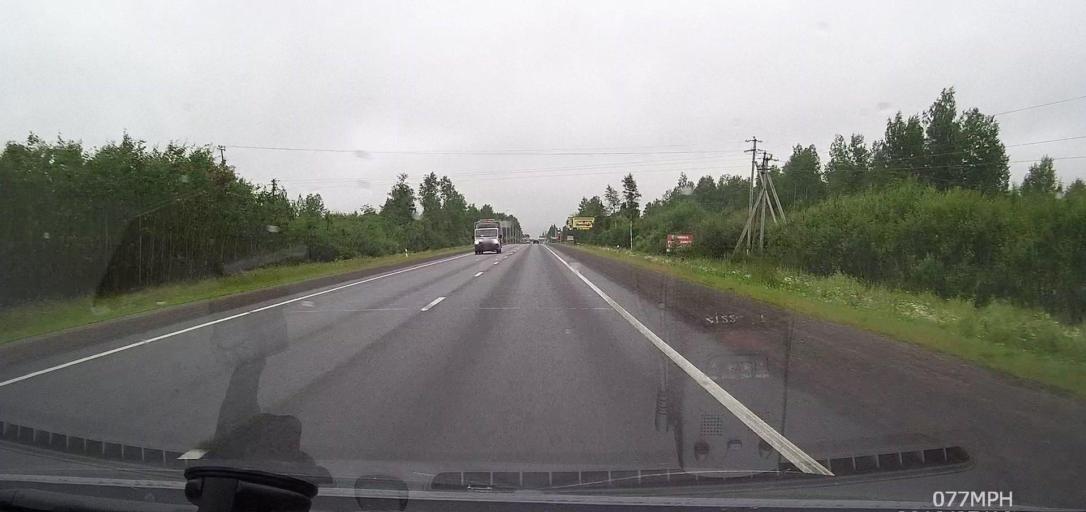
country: RU
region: Leningrad
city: Staraya Ladoga
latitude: 60.0029
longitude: 32.1214
